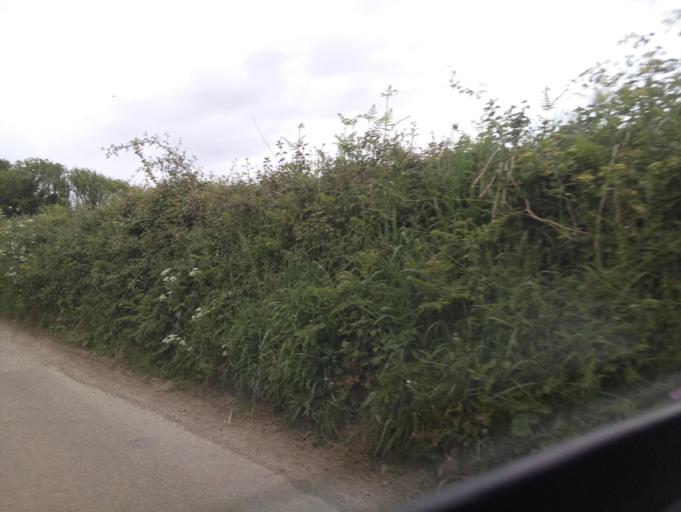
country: GB
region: England
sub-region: Devon
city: Dartmouth
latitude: 50.3333
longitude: -3.6474
